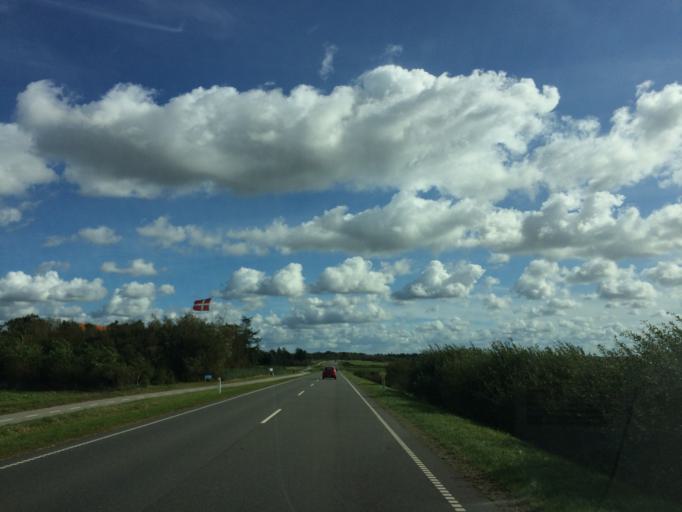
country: DK
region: Central Jutland
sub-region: Holstebro Kommune
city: Ulfborg
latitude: 56.2734
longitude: 8.2050
